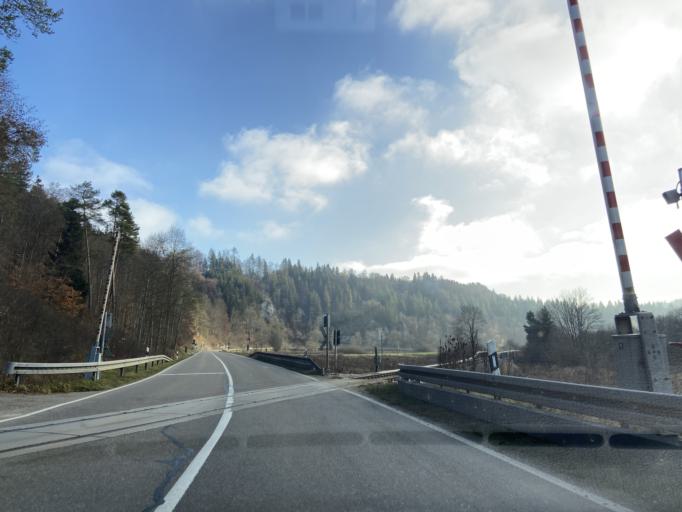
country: DE
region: Baden-Wuerttemberg
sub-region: Tuebingen Region
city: Gammertingen
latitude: 48.2347
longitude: 9.2252
